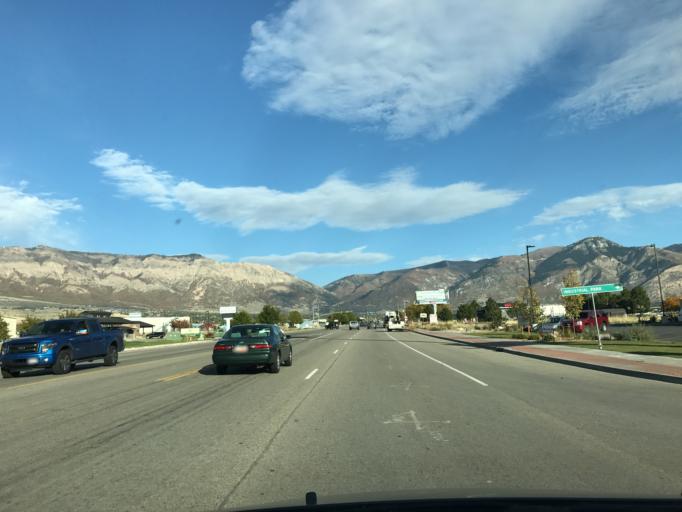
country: US
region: Utah
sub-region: Weber County
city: Farr West
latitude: 41.3067
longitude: -112.0190
